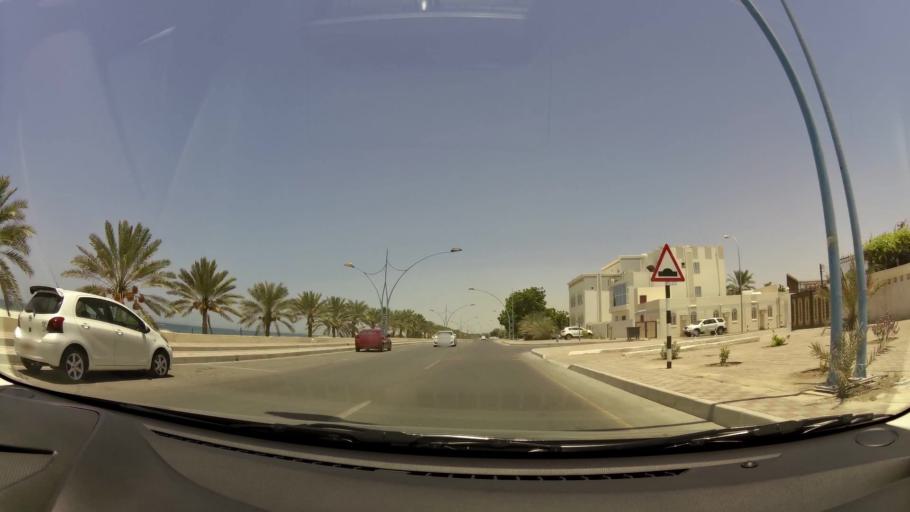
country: OM
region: Muhafazat Masqat
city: Bawshar
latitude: 23.6032
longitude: 58.3873
